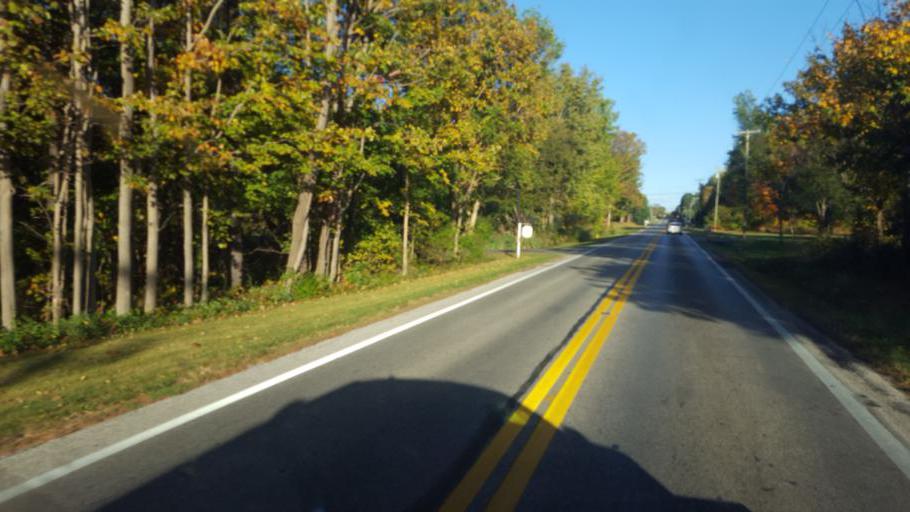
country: US
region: Ohio
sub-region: Franklin County
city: Gahanna
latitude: 40.0170
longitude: -82.8397
